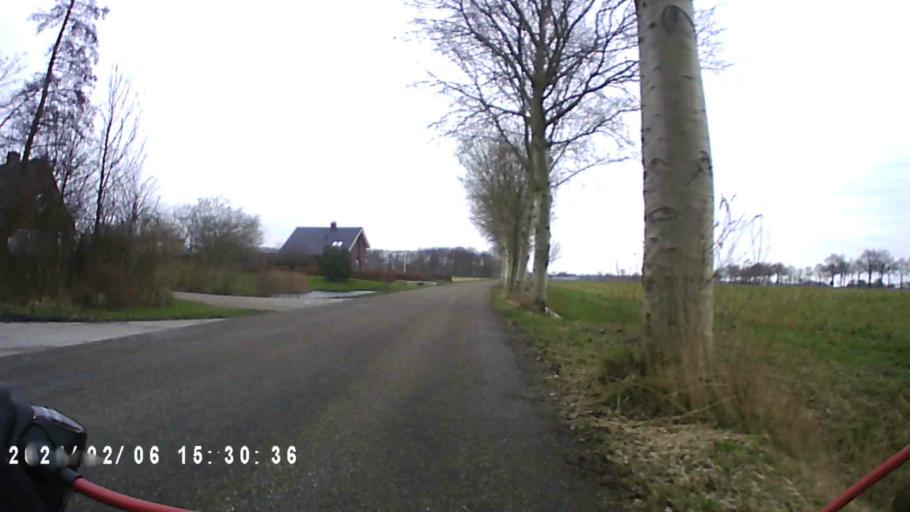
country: NL
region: Groningen
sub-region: Gemeente Bedum
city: Bedum
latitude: 53.4077
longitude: 6.6381
